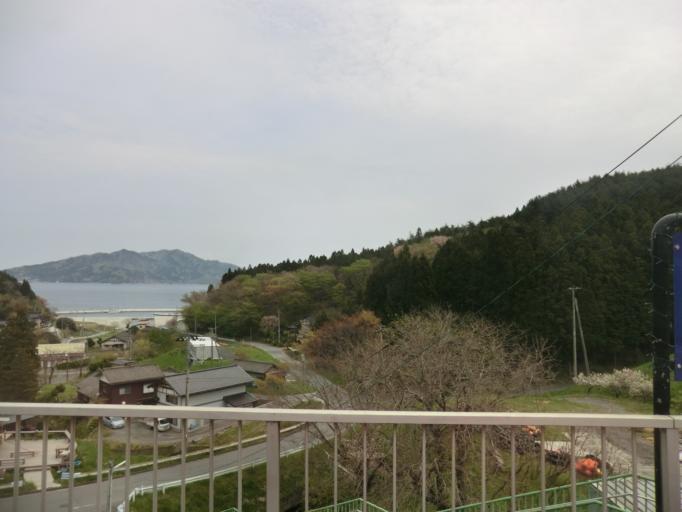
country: JP
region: Iwate
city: Ofunato
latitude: 39.0746
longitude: 141.8164
